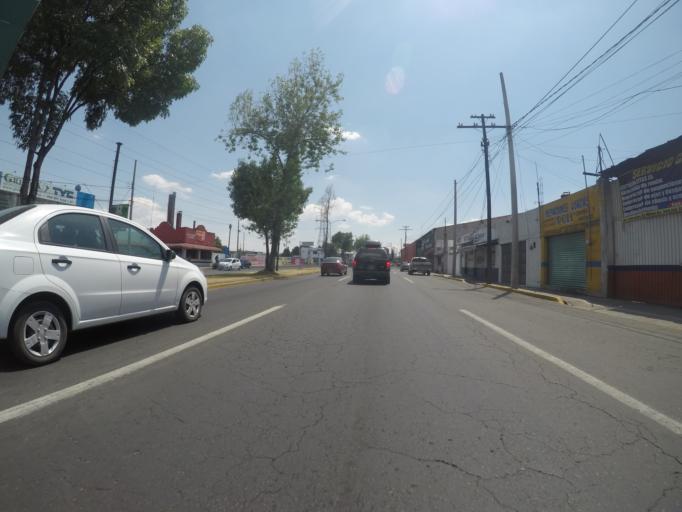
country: MX
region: Mexico
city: Toluca
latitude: 19.2789
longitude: -99.6316
